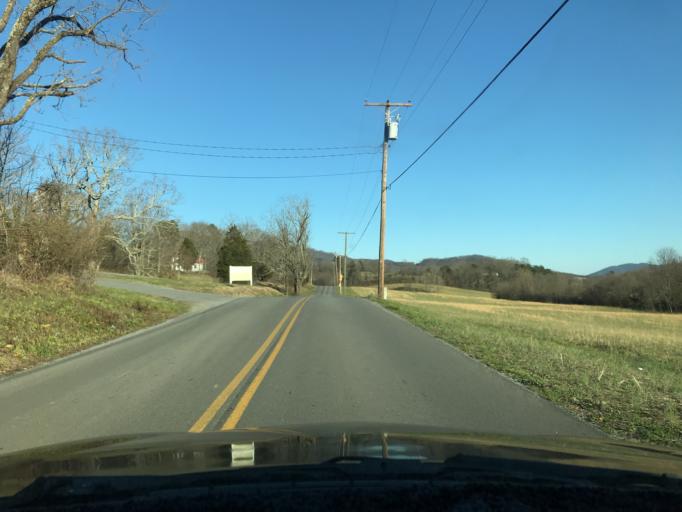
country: US
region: Virginia
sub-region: Botetourt County
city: Blue Ridge
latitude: 37.3901
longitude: -79.7242
